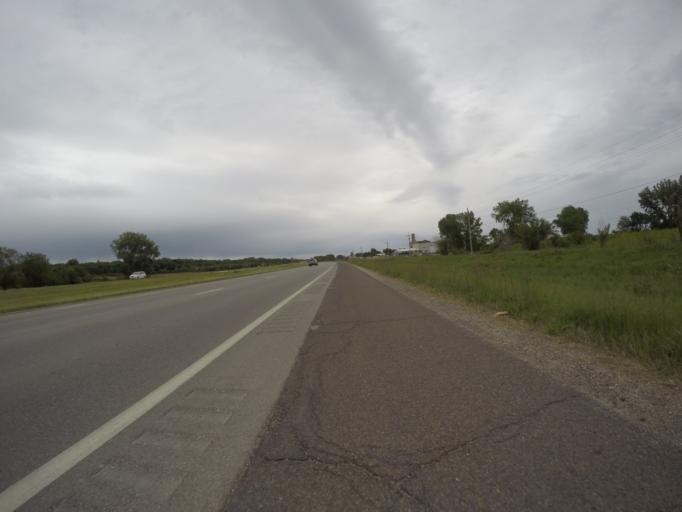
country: US
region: Kansas
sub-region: Riley County
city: Manhattan
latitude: 39.1961
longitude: -96.4933
